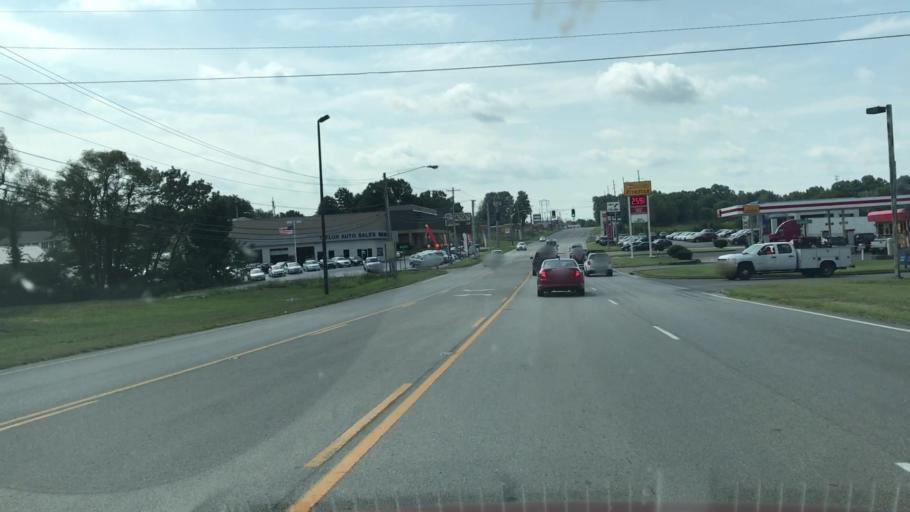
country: US
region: Kentucky
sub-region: Barren County
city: Glasgow
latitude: 37.0162
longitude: -85.9287
